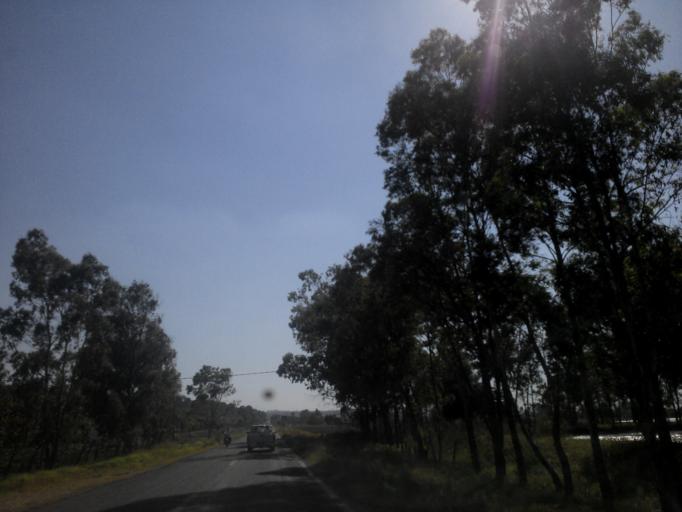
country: MX
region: Jalisco
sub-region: Arandas
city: Santiaguito (Santiaguito de Velazquez)
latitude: 20.7983
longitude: -102.2432
